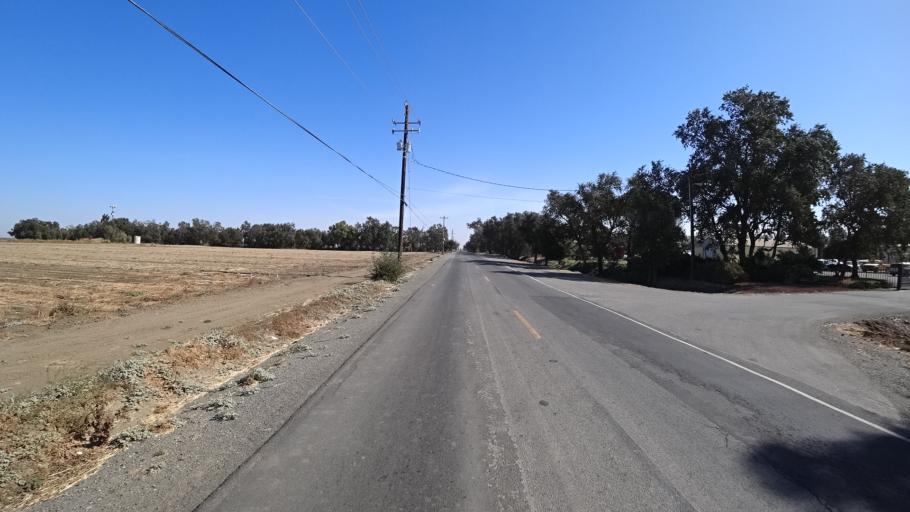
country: US
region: California
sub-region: Yolo County
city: Woodland
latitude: 38.6191
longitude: -121.7456
